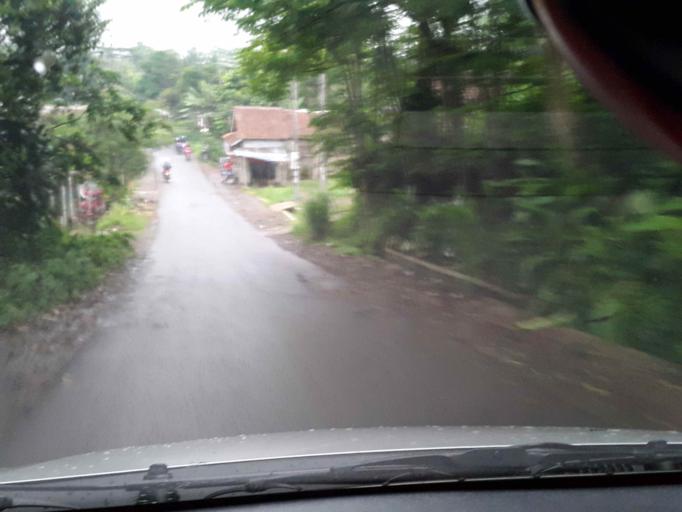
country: ID
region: West Java
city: Sukabumi
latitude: -6.9170
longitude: 106.8727
